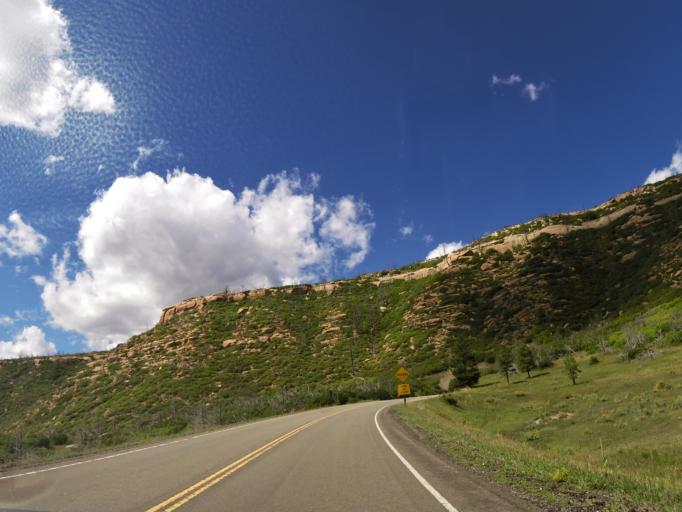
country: US
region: Colorado
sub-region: Montezuma County
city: Mancos
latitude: 37.2857
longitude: -108.4162
